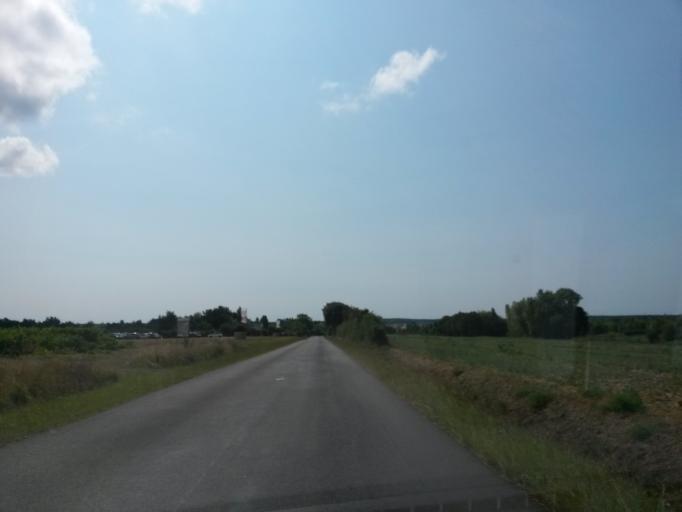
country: FR
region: Pays de la Loire
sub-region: Departement de la Vendee
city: Saint-Hilaire-de-Talmont
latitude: 46.4561
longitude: -1.6210
